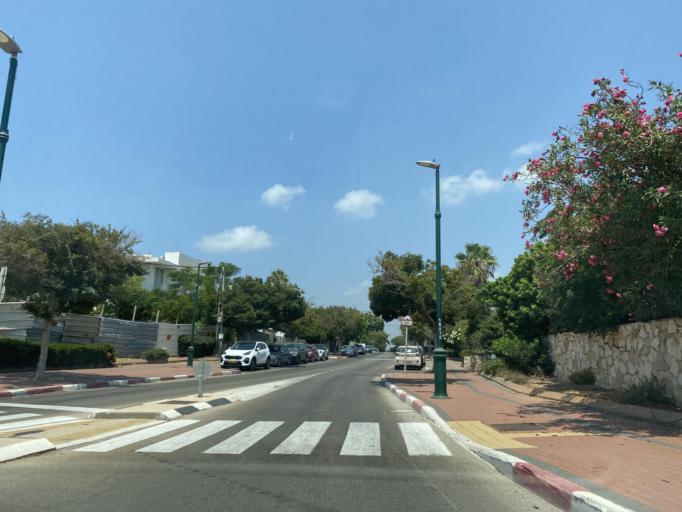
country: IL
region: Tel Aviv
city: Herzliya Pituah
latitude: 32.1754
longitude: 34.8043
